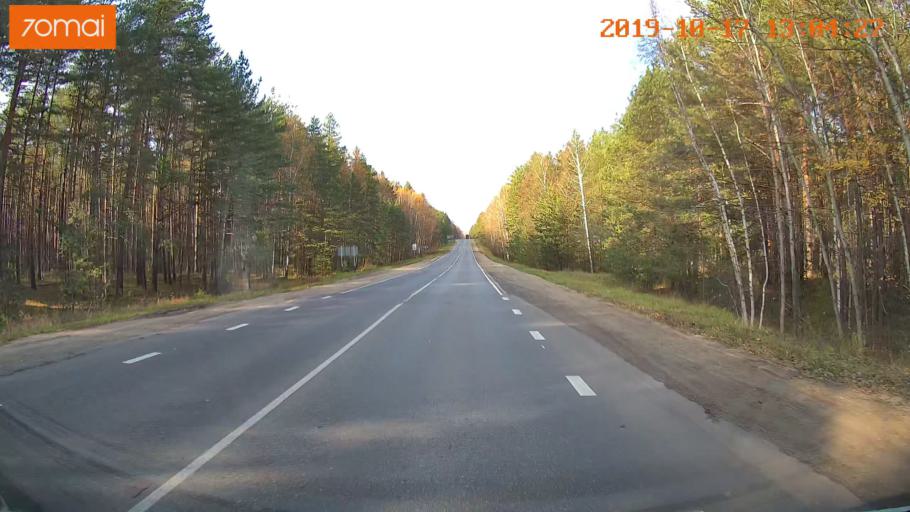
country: RU
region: Rjazan
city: Kasimov
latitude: 54.9618
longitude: 41.3437
